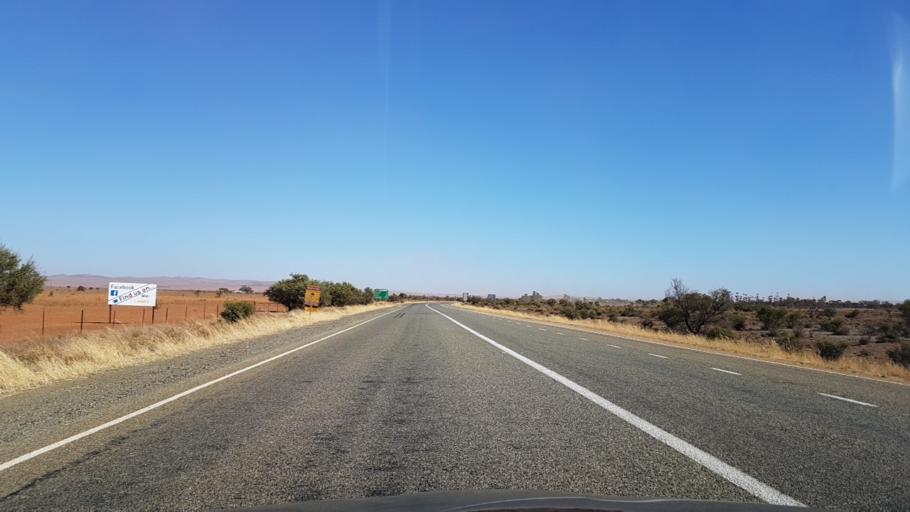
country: AU
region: South Australia
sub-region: Peterborough
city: Peterborough
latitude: -33.1354
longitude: 138.9342
